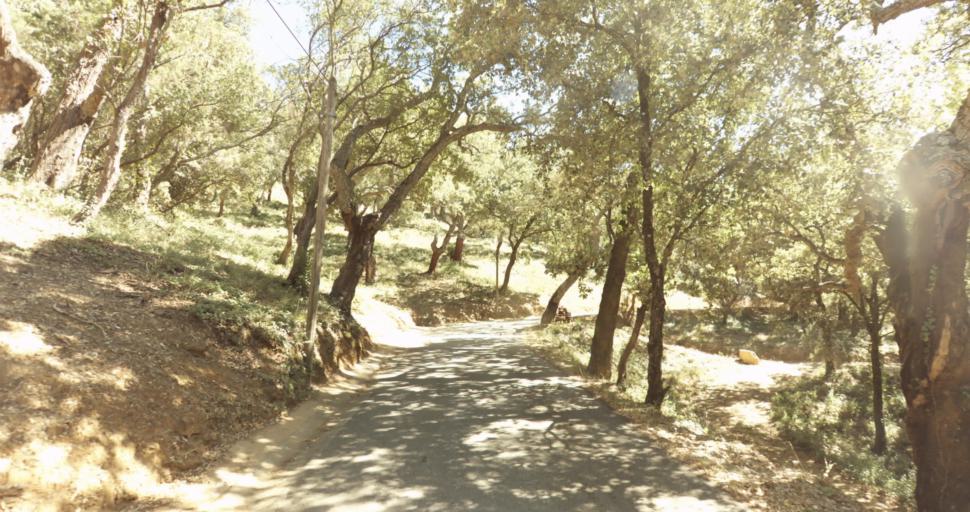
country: FR
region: Provence-Alpes-Cote d'Azur
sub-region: Departement du Var
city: La Croix-Valmer
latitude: 43.2269
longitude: 6.5603
